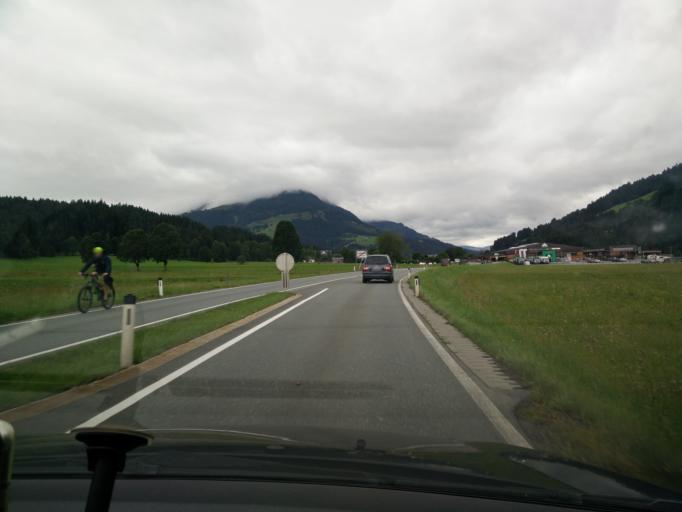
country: AT
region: Tyrol
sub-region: Politischer Bezirk Kitzbuhel
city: Reith bei Kitzbuhel
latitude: 47.4554
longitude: 12.3504
